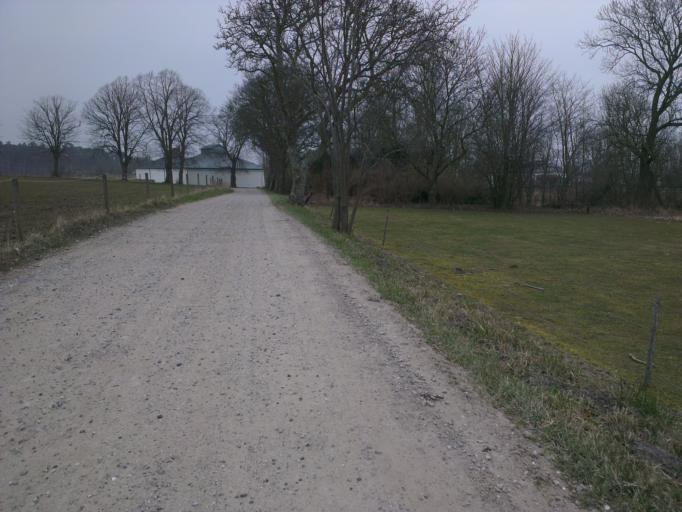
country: DK
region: Capital Region
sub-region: Frederikssund Kommune
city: Frederikssund
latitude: 55.7787
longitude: 12.0396
